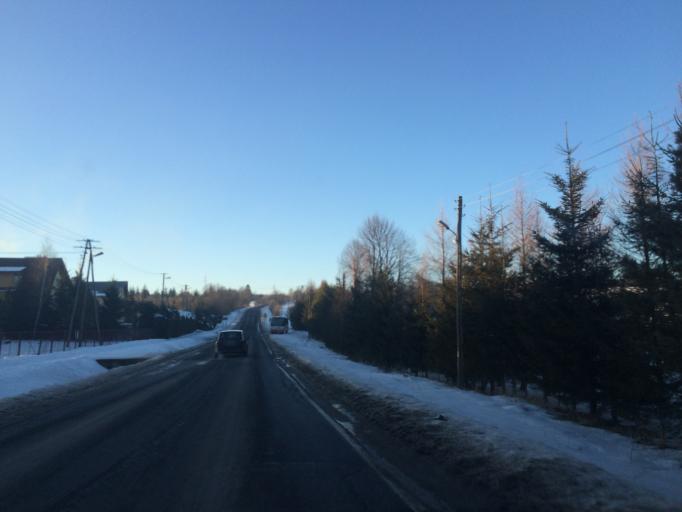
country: PL
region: Subcarpathian Voivodeship
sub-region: Powiat bieszczadzki
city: Lutowiska
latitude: 49.2555
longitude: 22.6888
